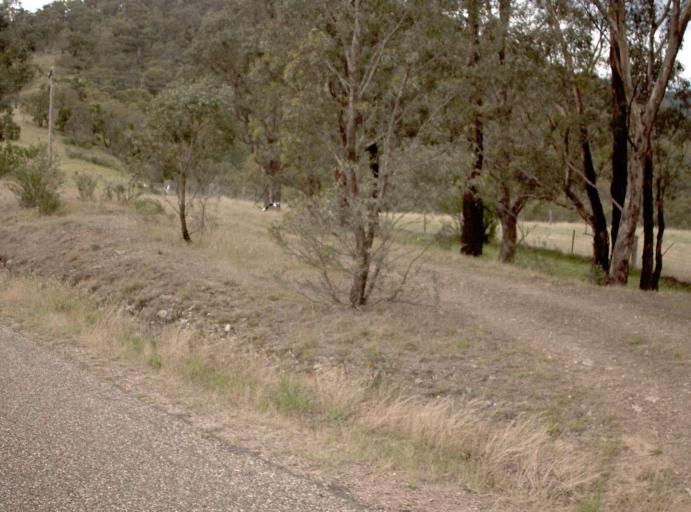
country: AU
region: Victoria
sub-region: East Gippsland
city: Bairnsdale
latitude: -37.5113
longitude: 147.2034
